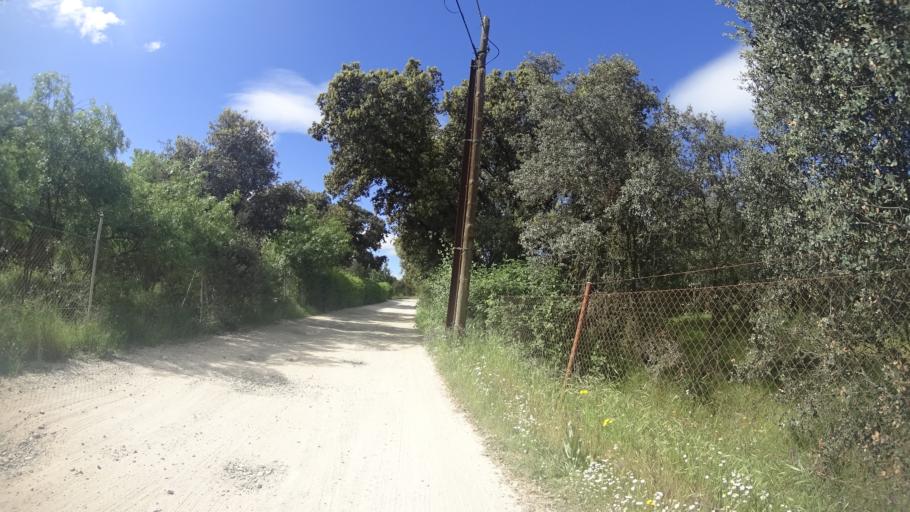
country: ES
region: Madrid
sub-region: Provincia de Madrid
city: Brunete
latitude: 40.4180
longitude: -3.9497
